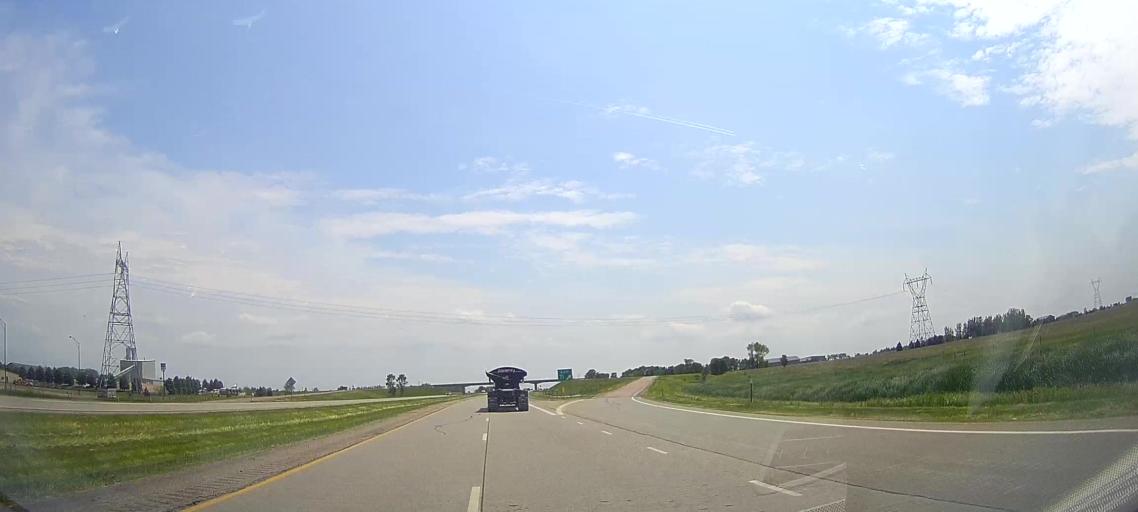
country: US
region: South Dakota
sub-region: Lincoln County
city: Tea
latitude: 43.4353
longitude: -96.7965
